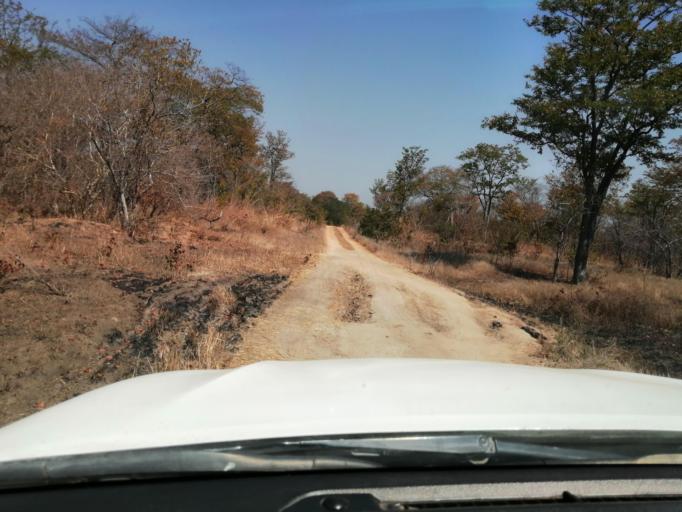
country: ZM
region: Eastern
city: Nyimba
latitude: -14.2535
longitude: 30.0924
